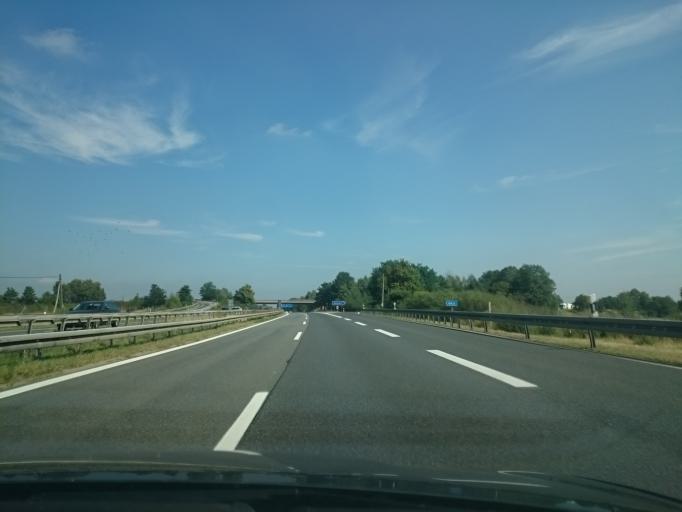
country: DE
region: Brandenburg
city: Lubbenau
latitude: 51.8287
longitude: 13.9095
